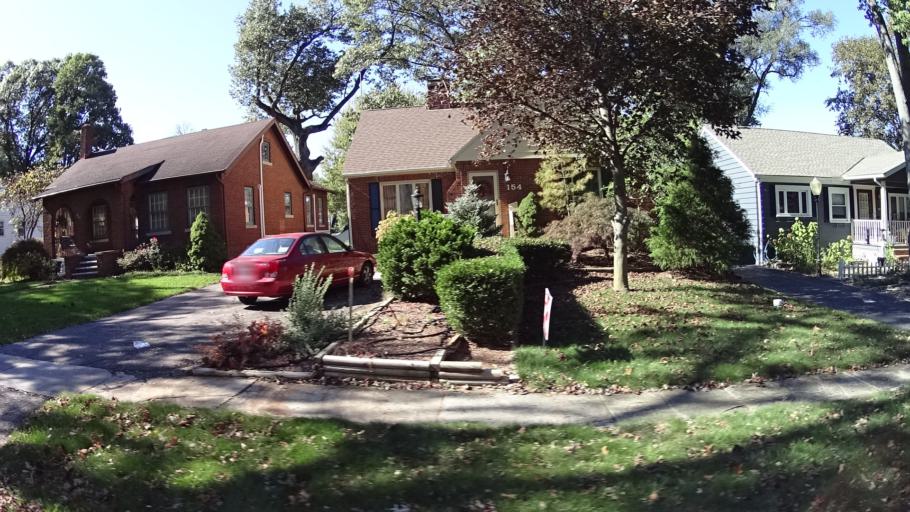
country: US
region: Ohio
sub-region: Lorain County
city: Amherst
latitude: 41.4006
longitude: -82.2156
